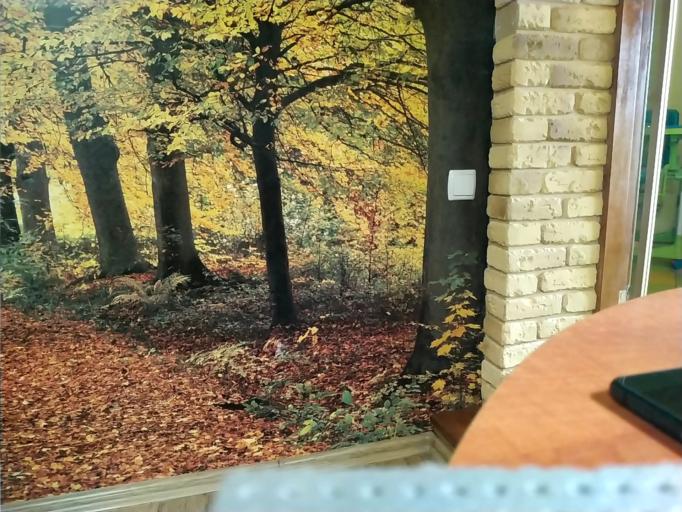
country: RU
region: Tverskaya
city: Likhoslavl'
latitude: 56.9917
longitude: 35.3874
